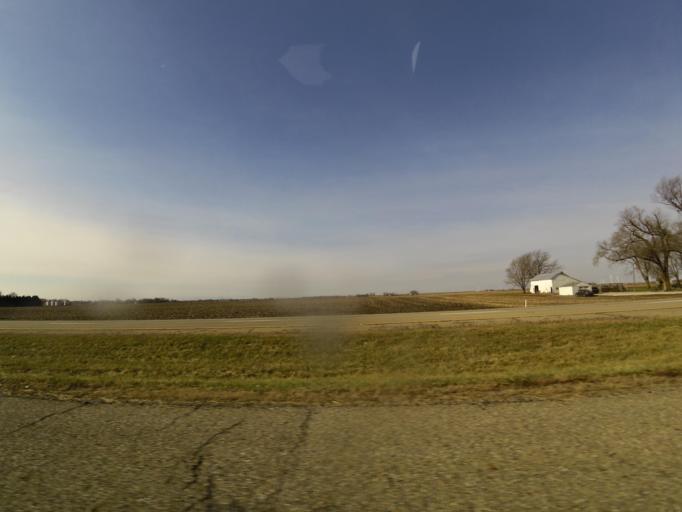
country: US
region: Illinois
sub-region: Macon County
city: Forsyth
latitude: 39.9416
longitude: -88.9554
